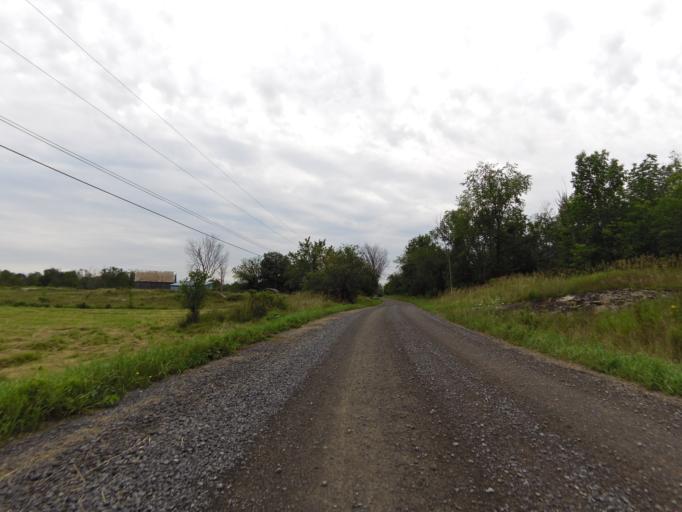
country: CA
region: Ontario
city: Perth
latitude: 44.6800
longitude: -76.6451
